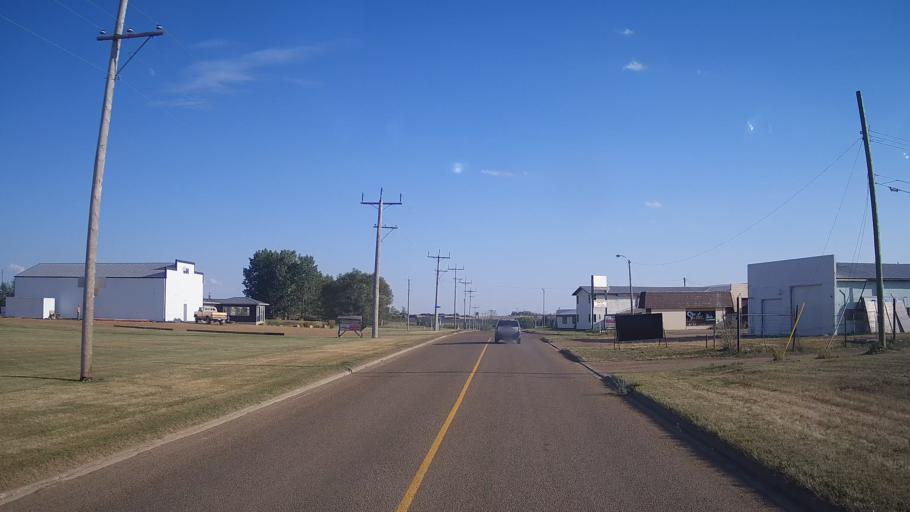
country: CA
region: Alberta
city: Hanna
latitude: 51.6447
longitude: -111.9185
